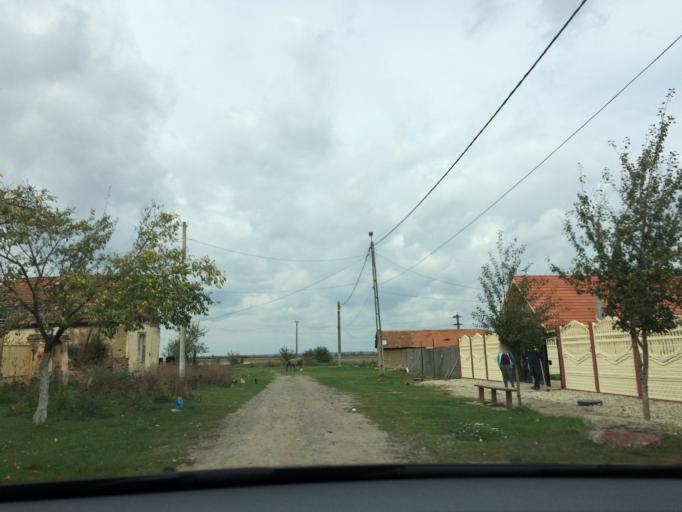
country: RO
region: Timis
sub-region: Oras Recas
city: Recas
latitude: 45.7433
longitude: 21.4922
